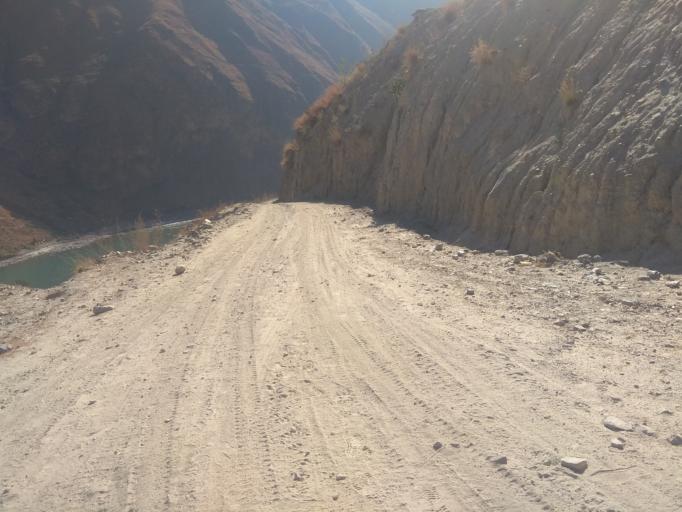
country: NP
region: Mid Western
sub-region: Karnali Zone
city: Jumla
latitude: 29.2970
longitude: 81.7462
